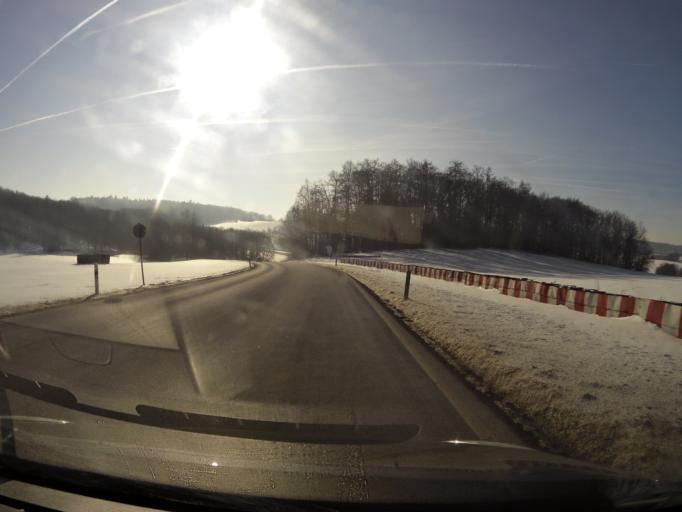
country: DE
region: Thuringia
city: Schleiz
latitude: 50.5646
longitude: 11.8078
